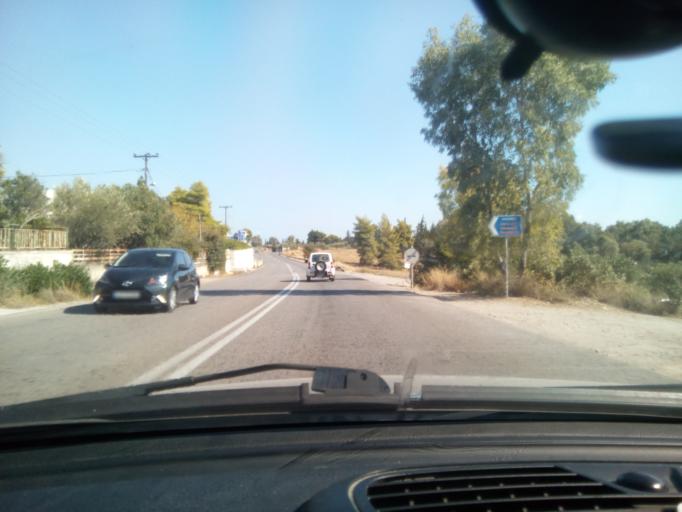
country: GR
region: Central Greece
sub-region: Nomos Evvoias
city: Malakonta
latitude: 38.4098
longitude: 23.7259
